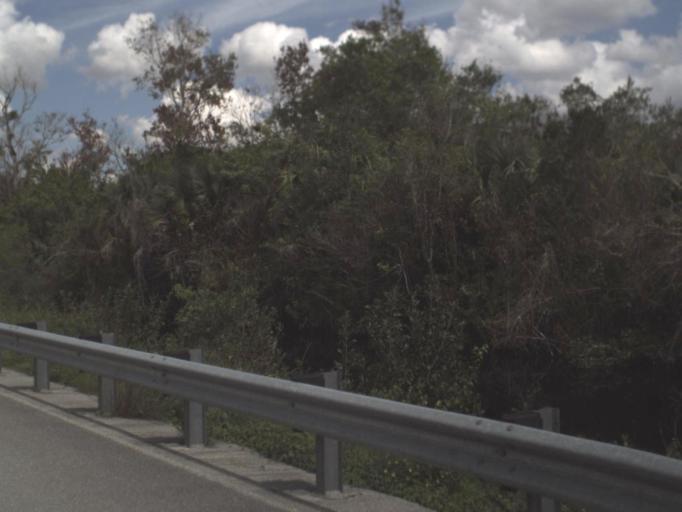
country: US
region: Florida
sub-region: Collier County
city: Lely Resort
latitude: 25.9325
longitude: -81.3574
